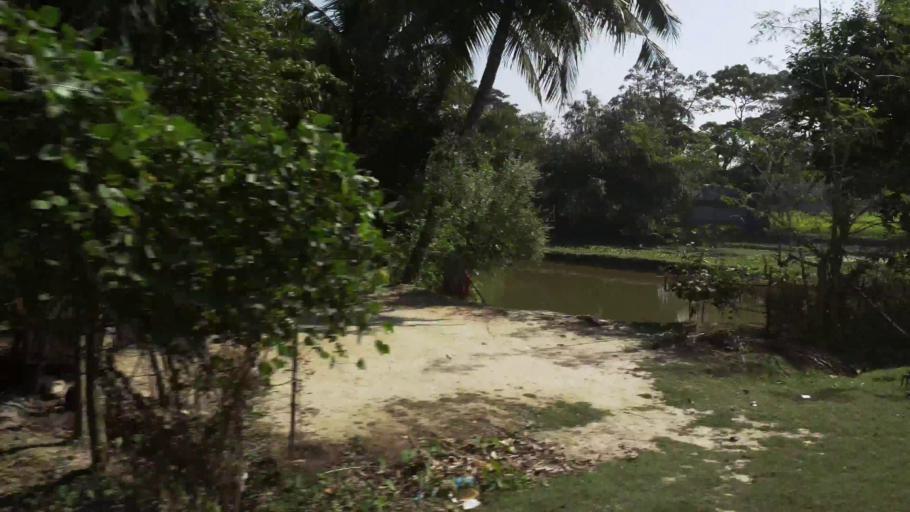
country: BD
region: Dhaka
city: Gafargaon
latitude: 24.5149
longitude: 90.5121
